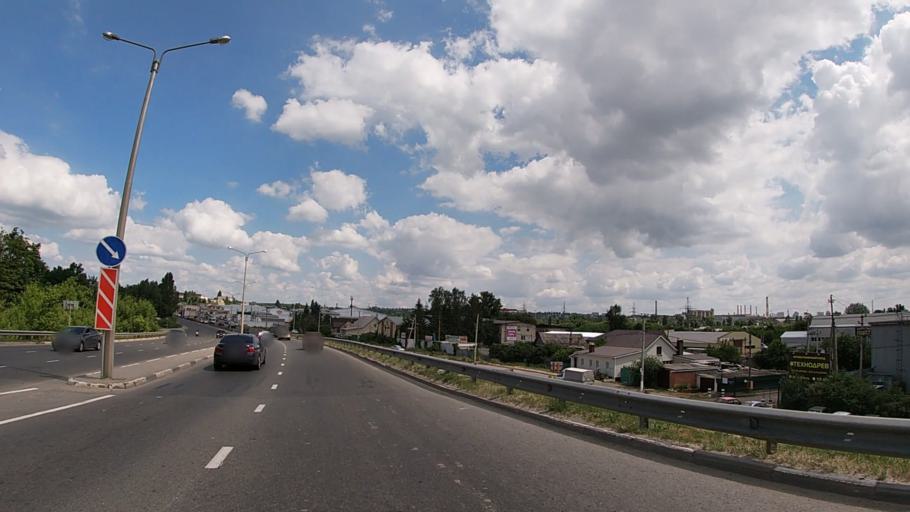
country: RU
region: Belgorod
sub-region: Belgorodskiy Rayon
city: Belgorod
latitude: 50.6081
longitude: 36.5332
